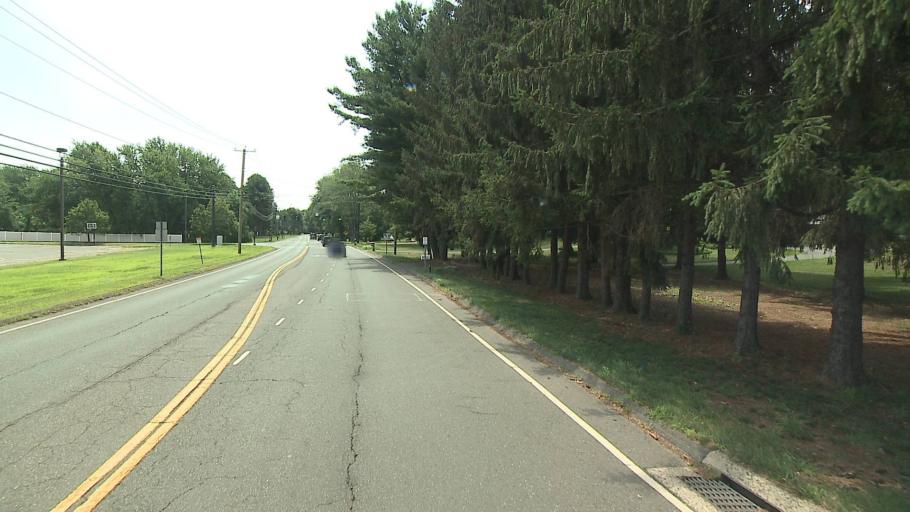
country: US
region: Connecticut
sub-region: Hartford County
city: Plainville
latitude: 41.7037
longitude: -72.8796
